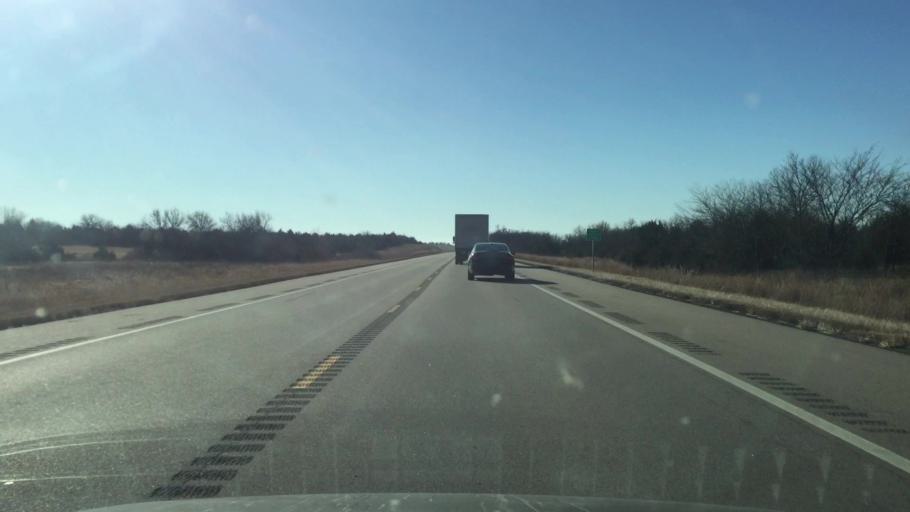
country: US
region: Kansas
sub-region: Allen County
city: Iola
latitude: 38.0381
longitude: -95.3806
